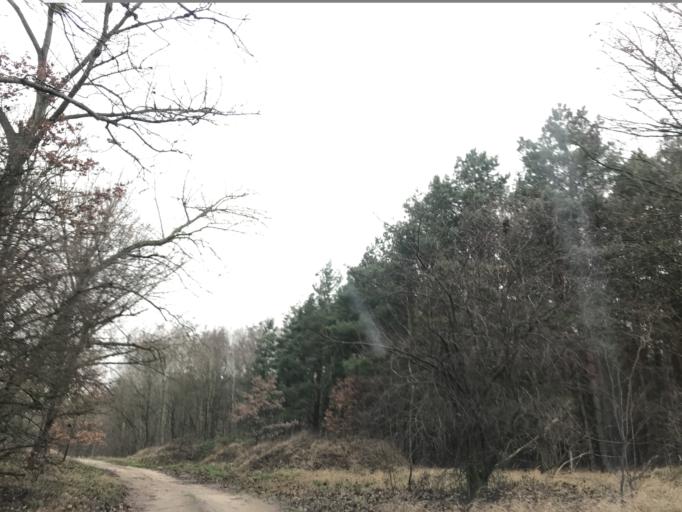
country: DE
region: Brandenburg
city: Kremmen
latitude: 52.7477
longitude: 12.9759
